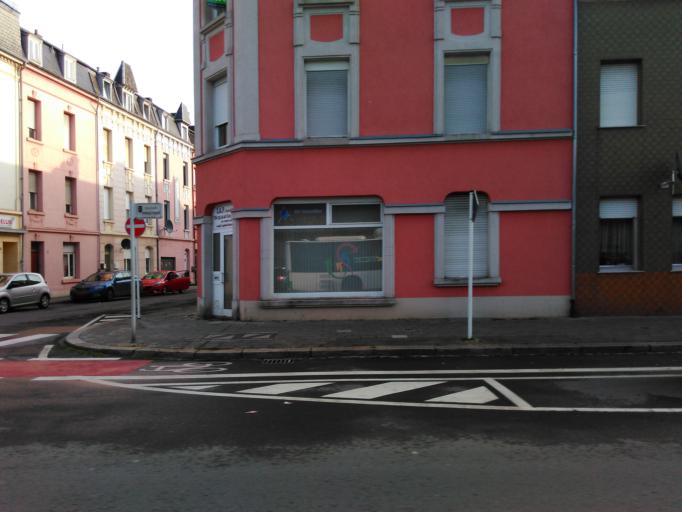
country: LU
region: Luxembourg
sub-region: Canton d'Esch-sur-Alzette
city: Esch-sur-Alzette
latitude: 49.4927
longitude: 5.9740
